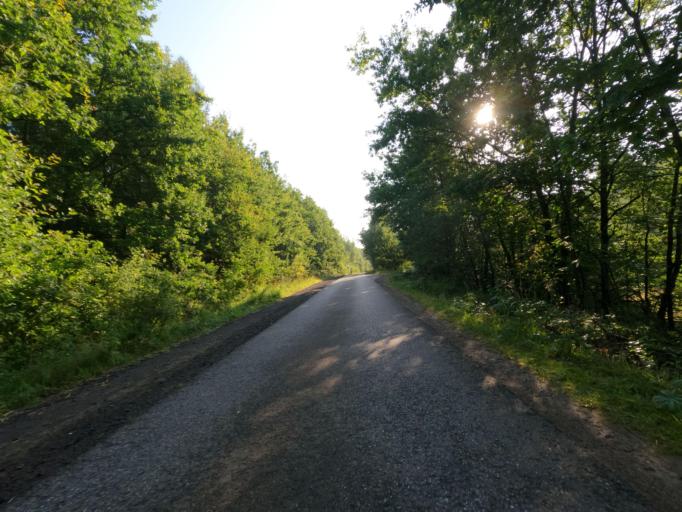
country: DE
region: North Rhine-Westphalia
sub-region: Regierungsbezirk Dusseldorf
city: Grevenbroich
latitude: 51.0505
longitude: 6.5472
